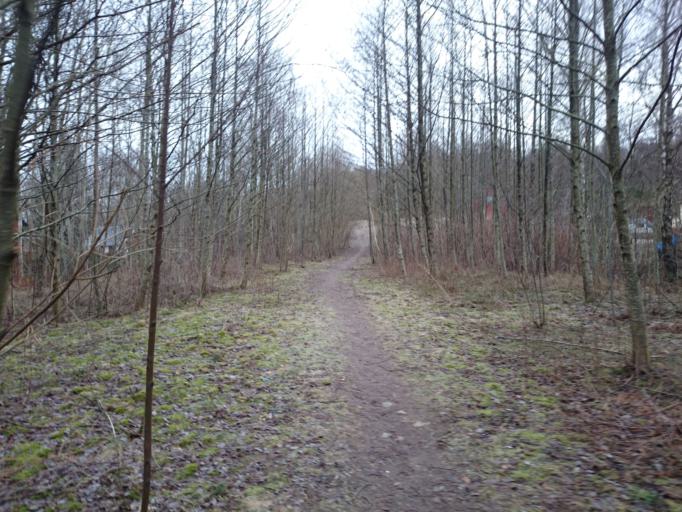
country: SE
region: Halland
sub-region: Hylte Kommun
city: Hyltebruk
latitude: 56.9952
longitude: 13.2396
